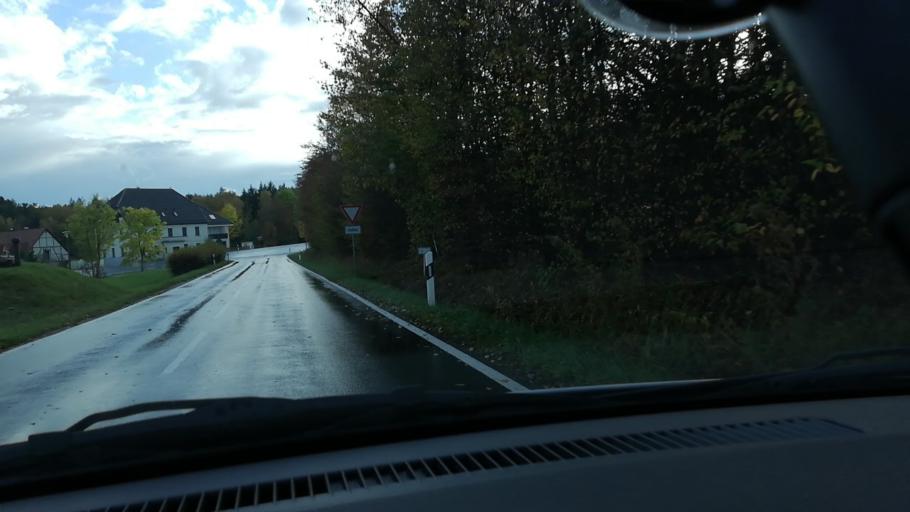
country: DE
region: Bavaria
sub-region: Regierungsbezirk Unterfranken
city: Rechtenbach
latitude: 49.9798
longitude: 9.4626
